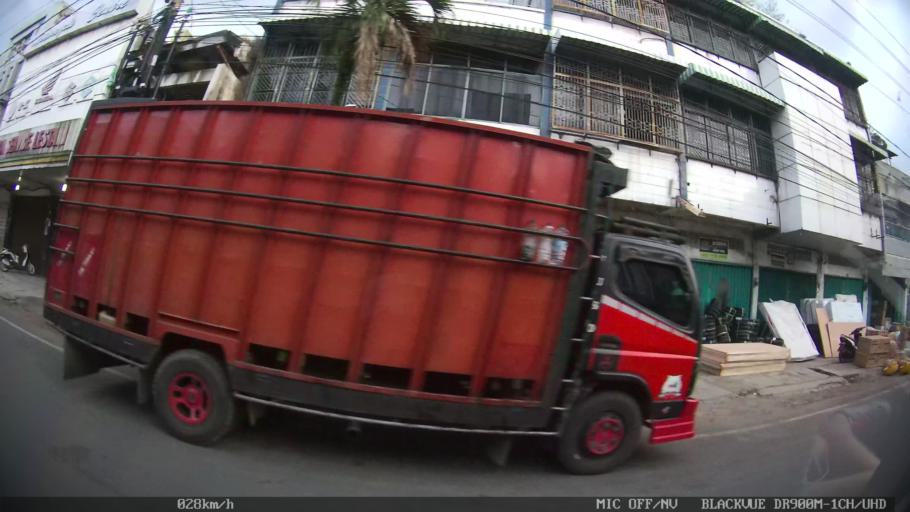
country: ID
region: North Sumatra
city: Medan
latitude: 3.5812
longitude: 98.6934
